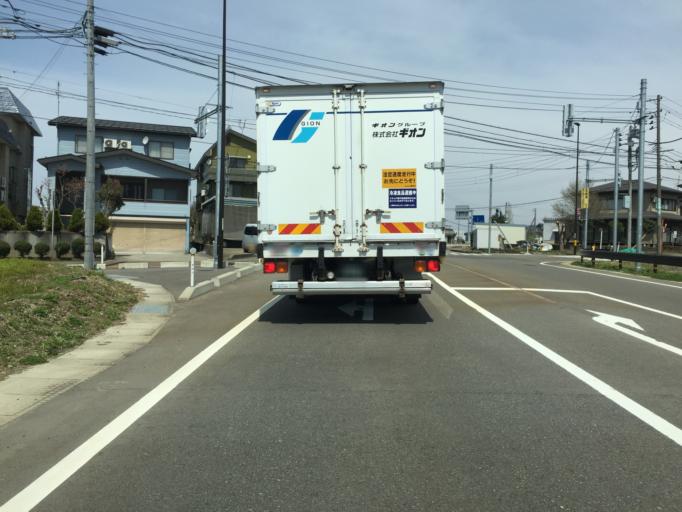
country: JP
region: Niigata
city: Ojiya
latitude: 37.3299
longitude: 138.8114
